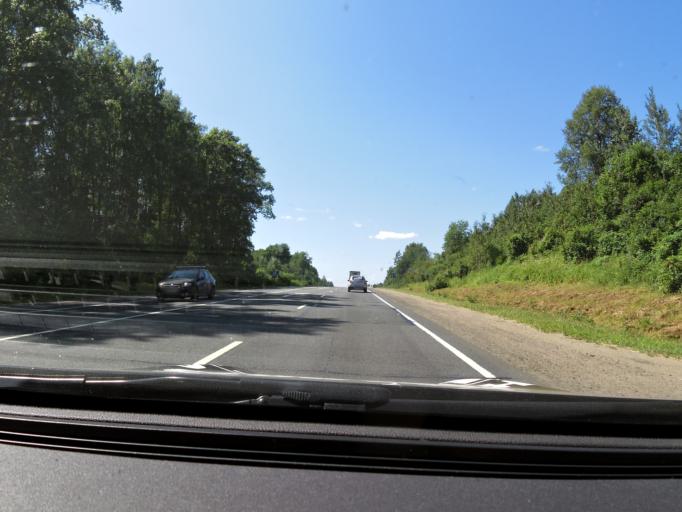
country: RU
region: Novgorod
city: Valday
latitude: 58.0259
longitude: 33.0236
